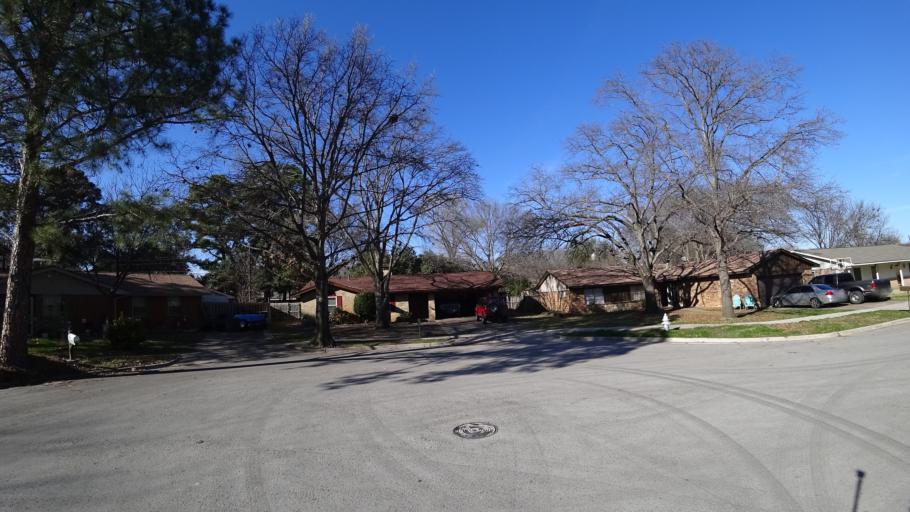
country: US
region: Texas
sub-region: Denton County
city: Lewisville
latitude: 33.0743
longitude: -97.0128
